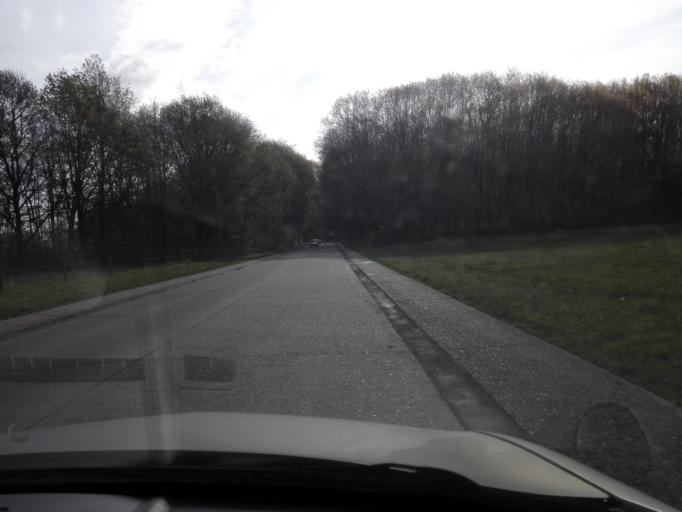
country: BE
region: Flanders
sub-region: Provincie Vlaams-Brabant
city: Aarschot
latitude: 50.9673
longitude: 4.8435
